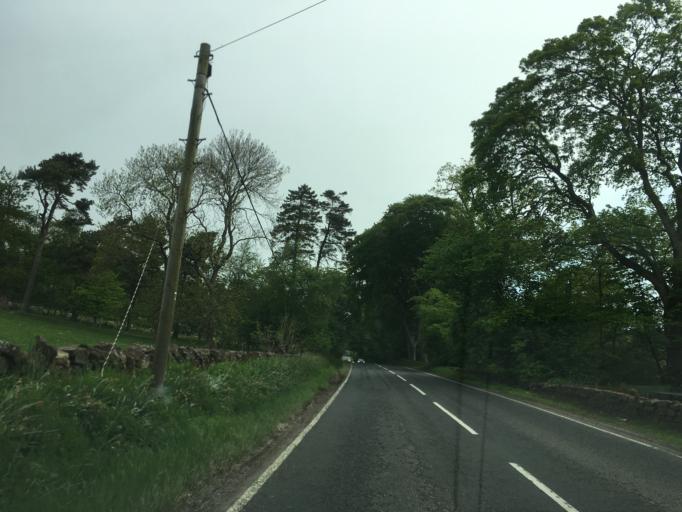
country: GB
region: Scotland
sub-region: The Scottish Borders
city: West Linton
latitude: 55.6991
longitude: -3.3681
